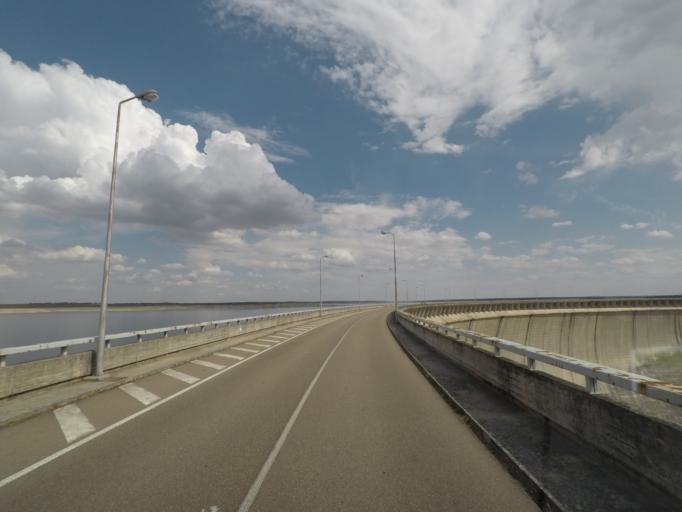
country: ES
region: Castille and Leon
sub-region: Provincia de Salamanca
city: Almendra
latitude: 41.2728
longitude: -6.3221
